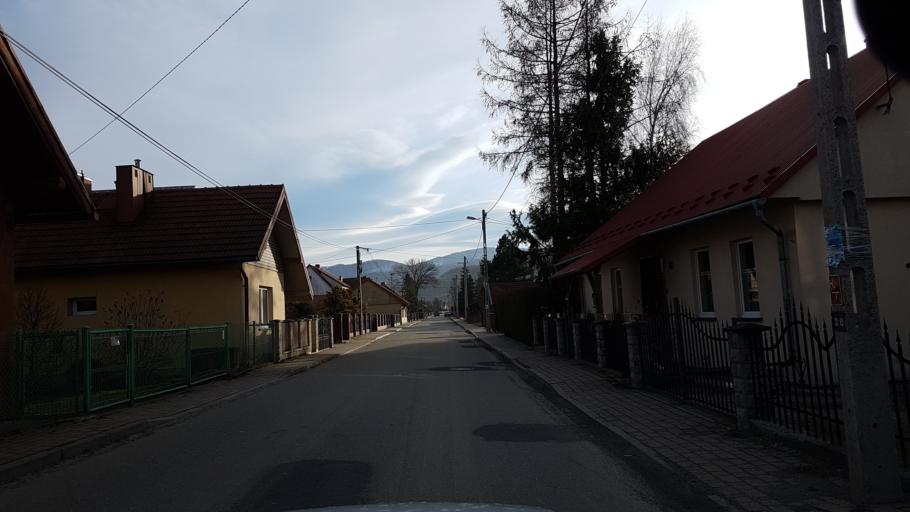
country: PL
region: Lesser Poland Voivodeship
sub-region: Powiat nowosadecki
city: Stary Sacz
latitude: 49.5340
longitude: 20.6545
